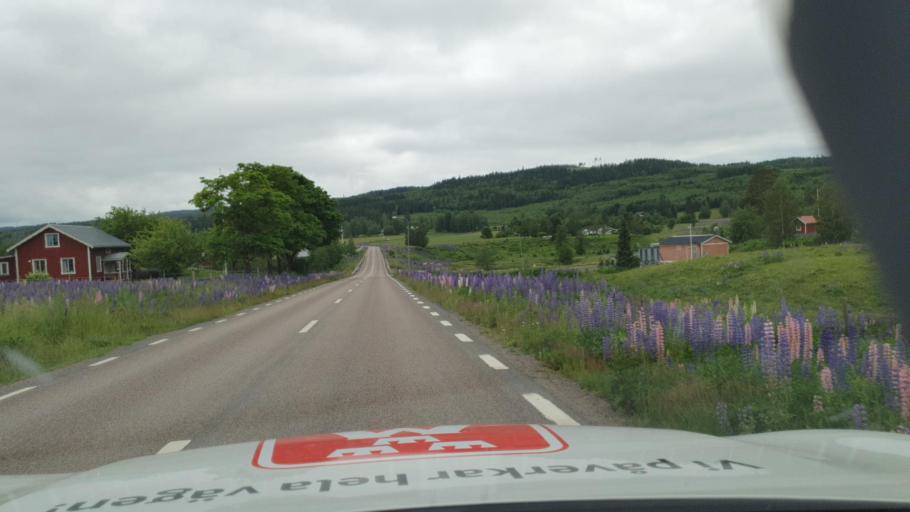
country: SE
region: Vaermland
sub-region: Sunne Kommun
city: Sunne
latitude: 59.8539
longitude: 12.9458
